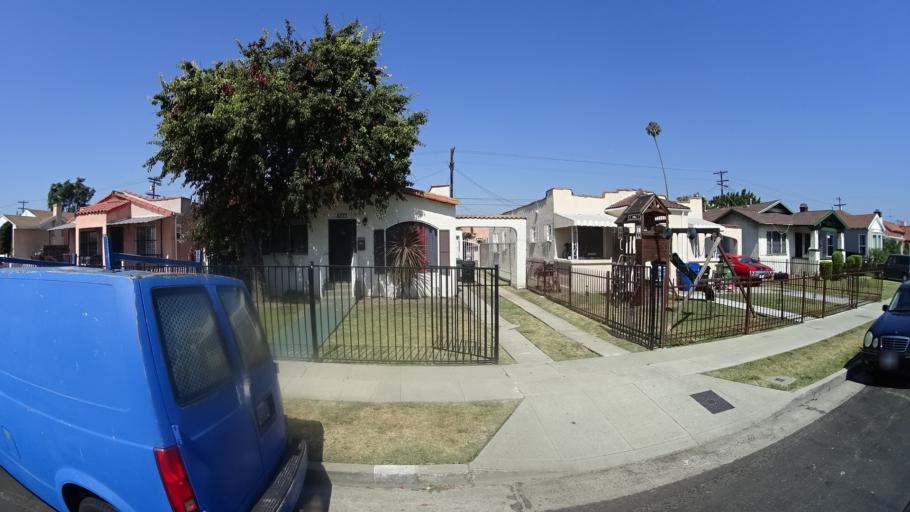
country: US
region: California
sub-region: Los Angeles County
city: View Park-Windsor Hills
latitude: 33.9830
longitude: -118.3219
